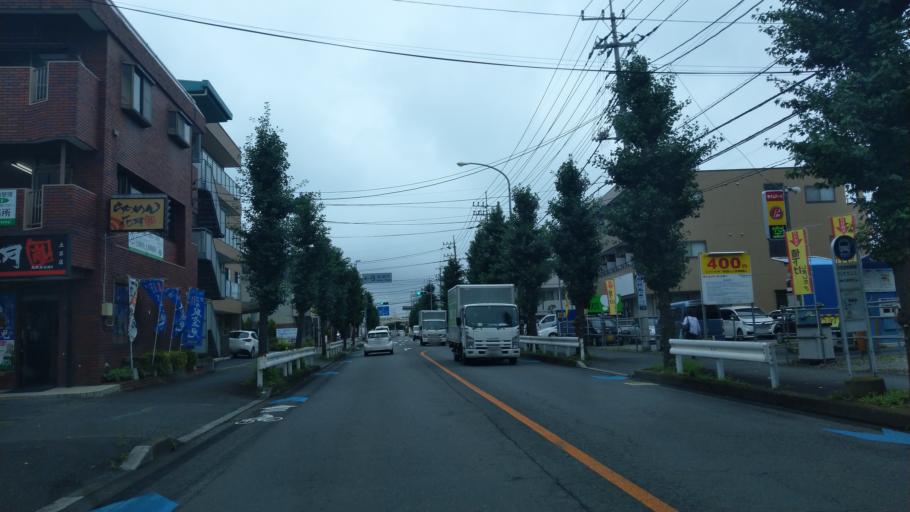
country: JP
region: Saitama
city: Saitama
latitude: 35.9291
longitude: 139.6347
